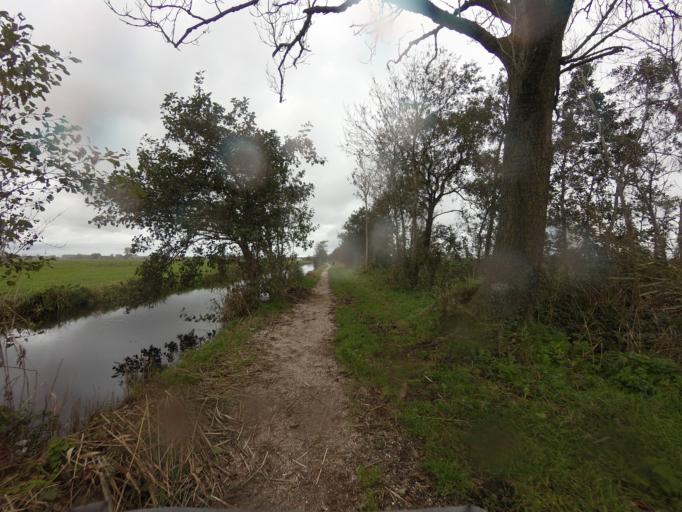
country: NL
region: South Holland
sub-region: Gemeente Alphen aan den Rijn
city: Alphen aan den Rijn
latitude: 52.1029
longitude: 4.6515
